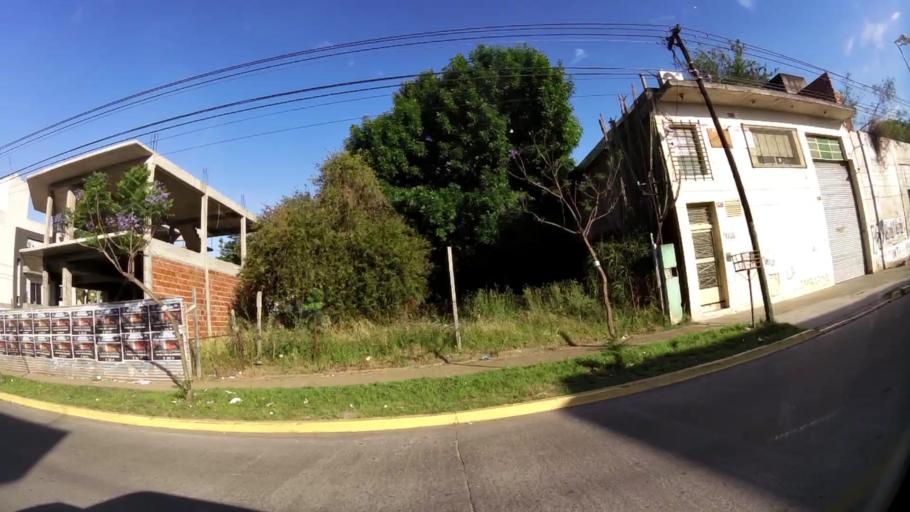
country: AR
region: Buenos Aires
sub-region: Partido de Merlo
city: Merlo
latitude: -34.6783
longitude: -58.7268
